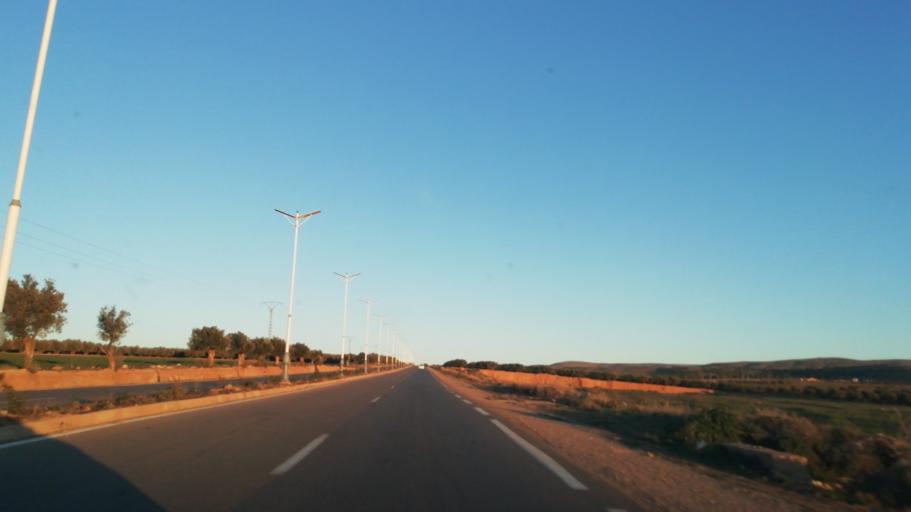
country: DZ
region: Saida
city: Saida
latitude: 34.8653
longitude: 0.1846
